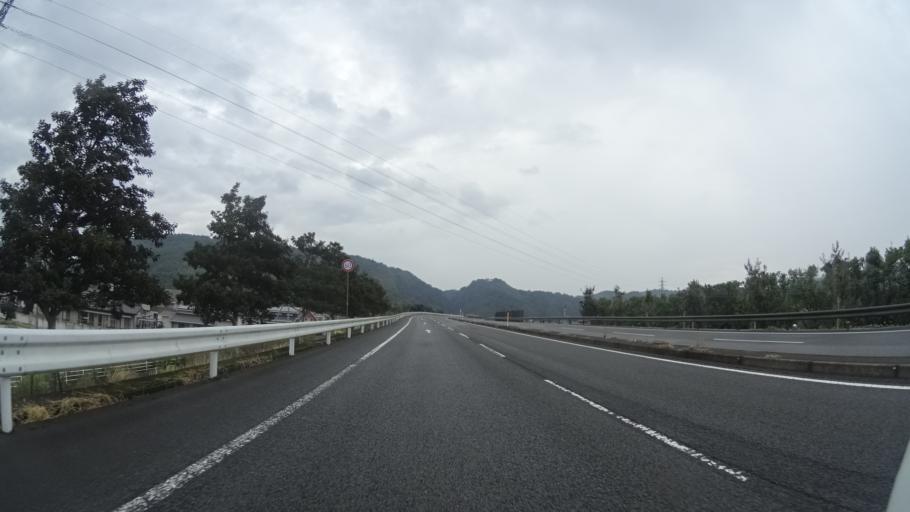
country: JP
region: Kagoshima
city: Kajiki
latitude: 31.7471
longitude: 130.6577
